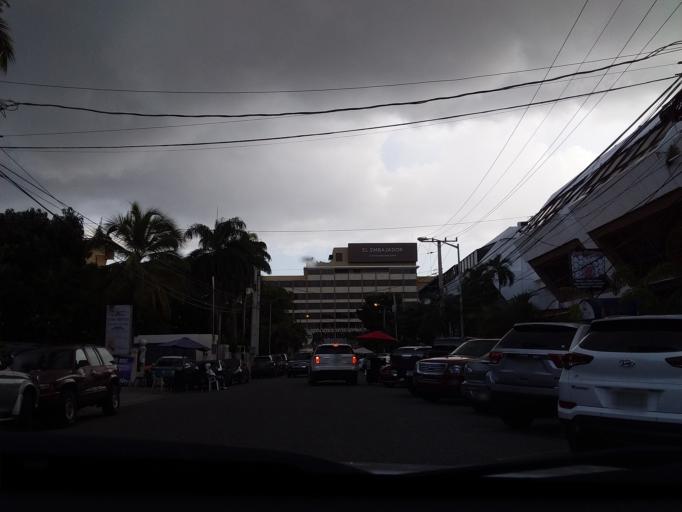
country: DO
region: Nacional
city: La Julia
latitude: 18.4567
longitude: -69.9344
